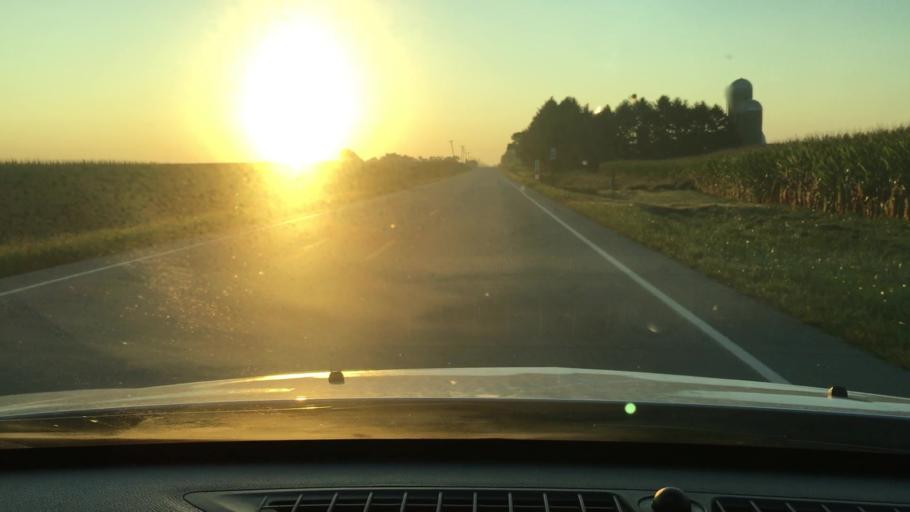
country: US
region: Illinois
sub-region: DeKalb County
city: Malta
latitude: 41.8485
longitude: -88.8630
